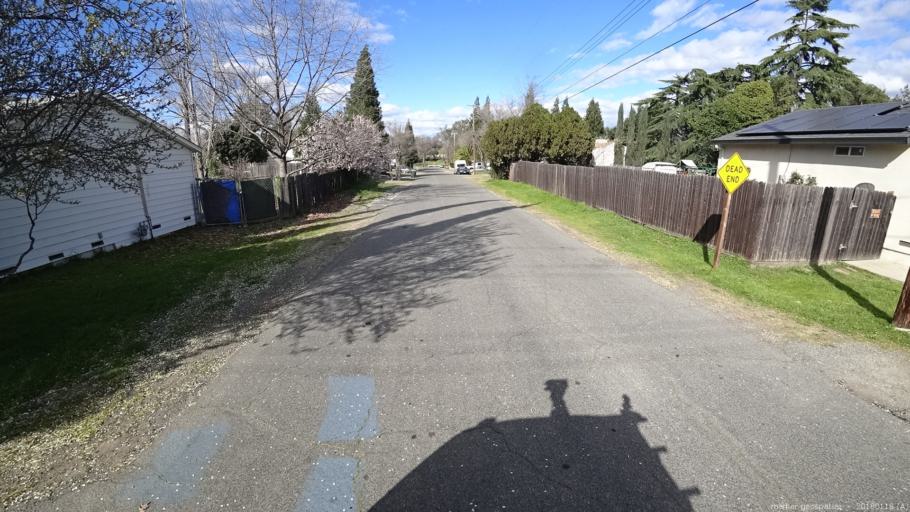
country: US
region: California
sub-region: Sacramento County
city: Orangevale
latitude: 38.7001
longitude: -121.2081
